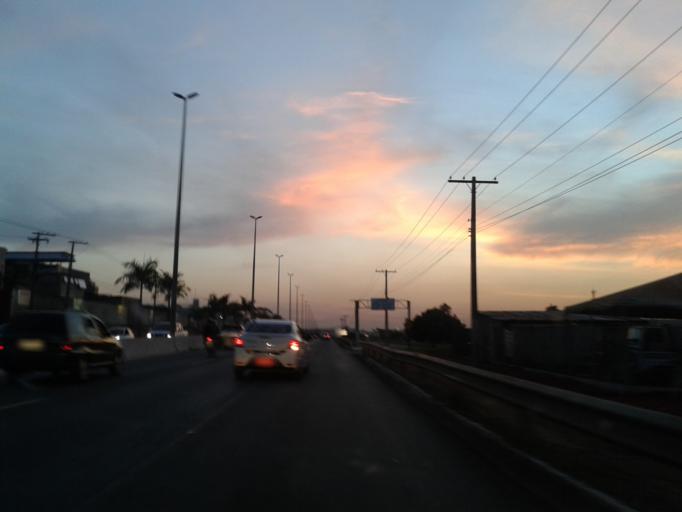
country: BR
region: Goias
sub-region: Goiania
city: Goiania
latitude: -16.6598
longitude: -49.3431
